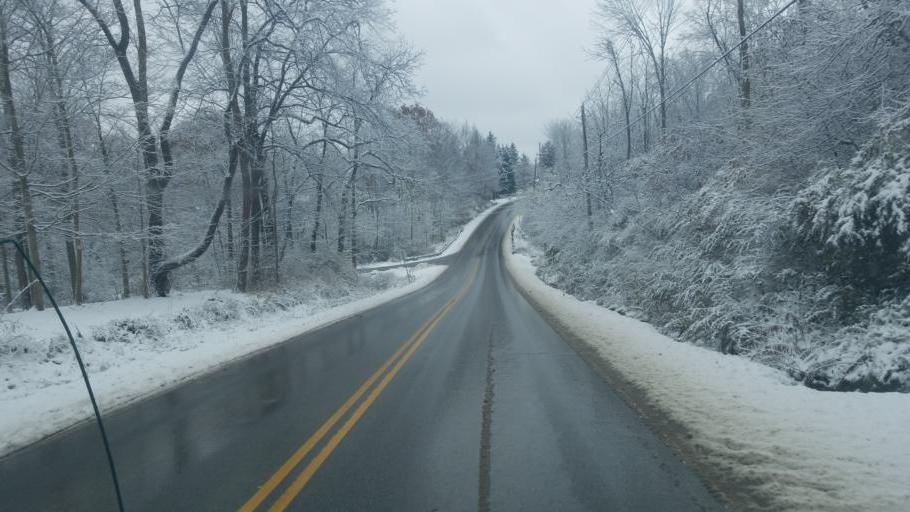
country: US
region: Ohio
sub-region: Geauga County
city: Middlefield
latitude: 41.4341
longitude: -81.0543
